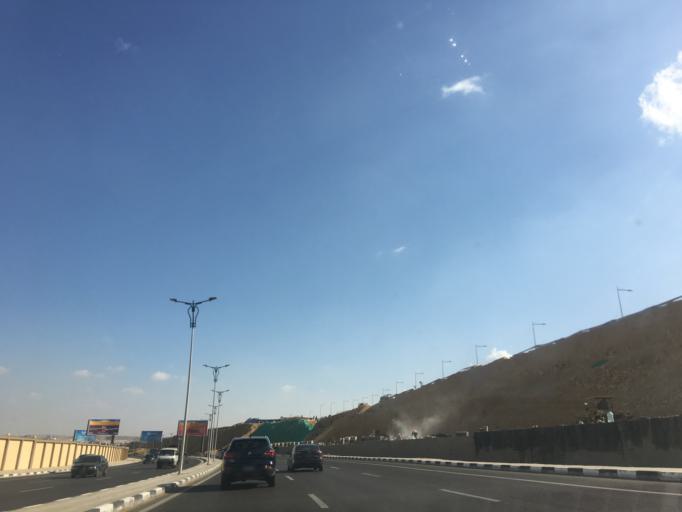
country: EG
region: Muhafazat al Qahirah
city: Cairo
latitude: 30.0288
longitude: 31.3114
